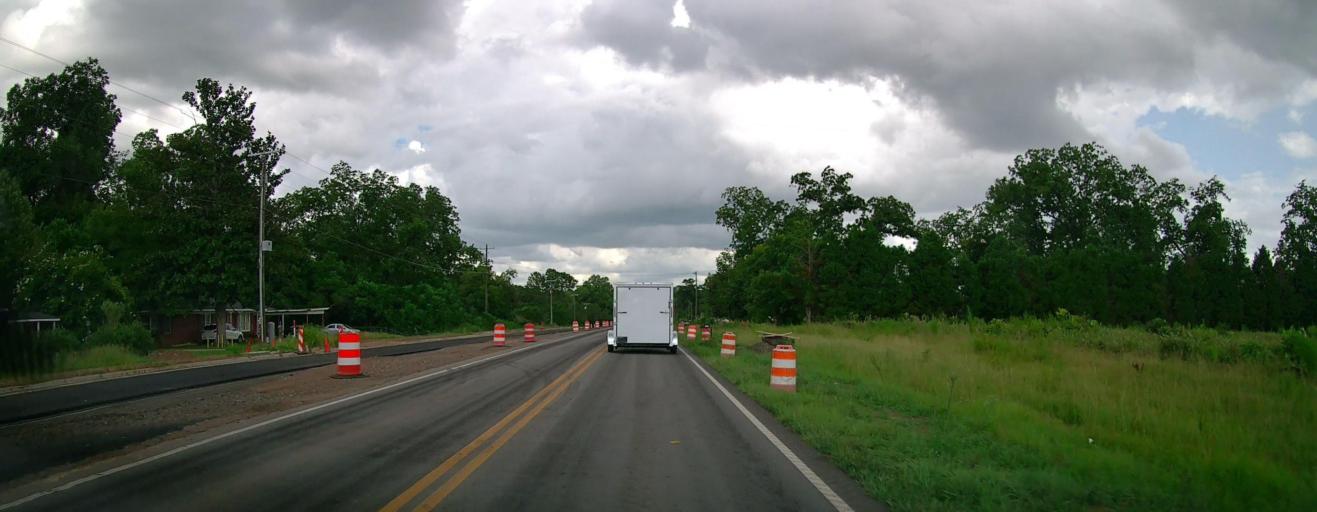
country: US
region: Georgia
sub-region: Coffee County
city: Douglas
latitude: 31.5179
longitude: -82.8845
